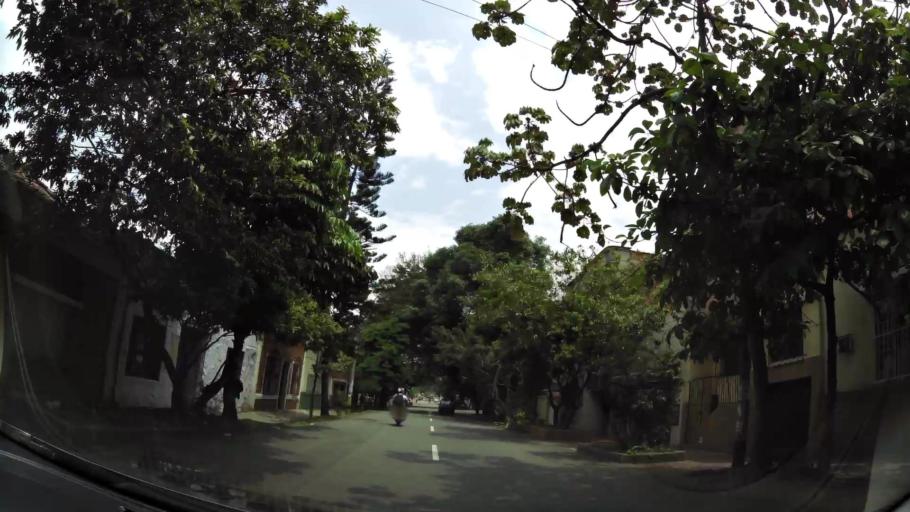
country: CO
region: Antioquia
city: Medellin
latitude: 6.2625
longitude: -75.5627
